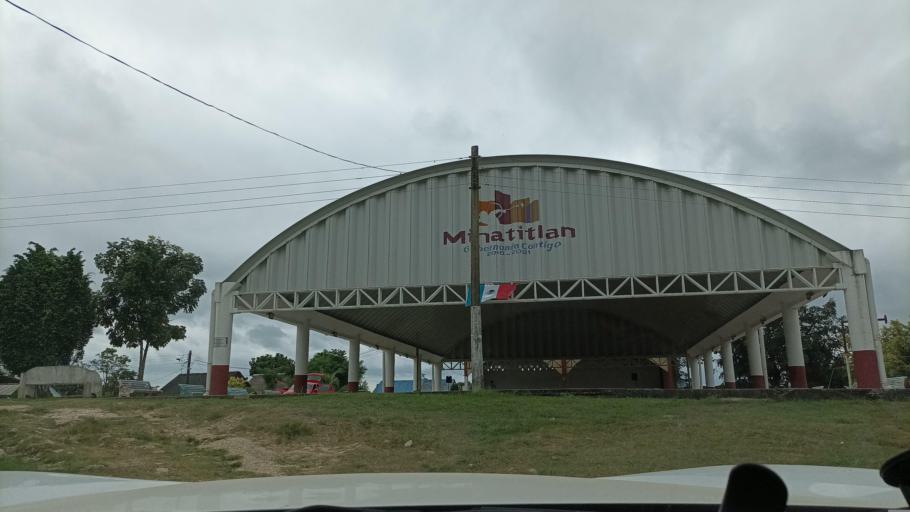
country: MX
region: Veracruz
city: Hidalgotitlan
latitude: 17.8089
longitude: -94.5414
